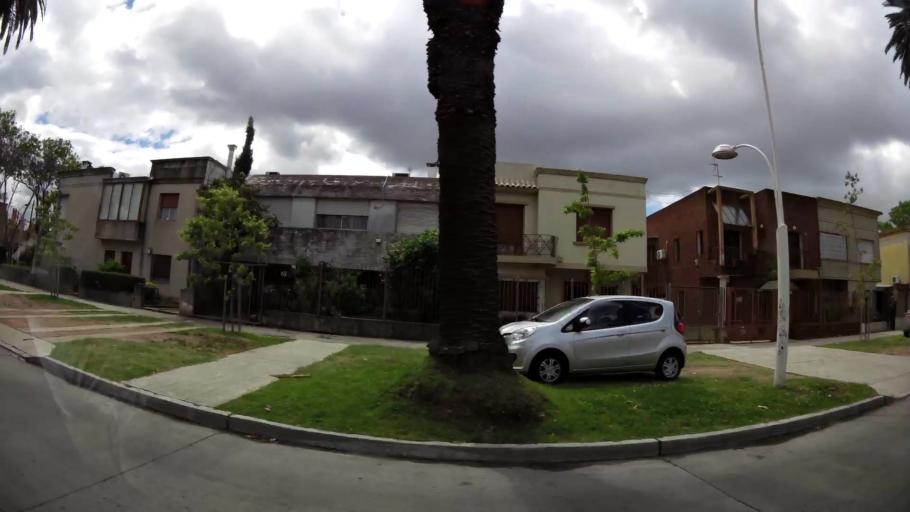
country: UY
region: Montevideo
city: Montevideo
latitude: -34.8760
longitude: -56.1669
